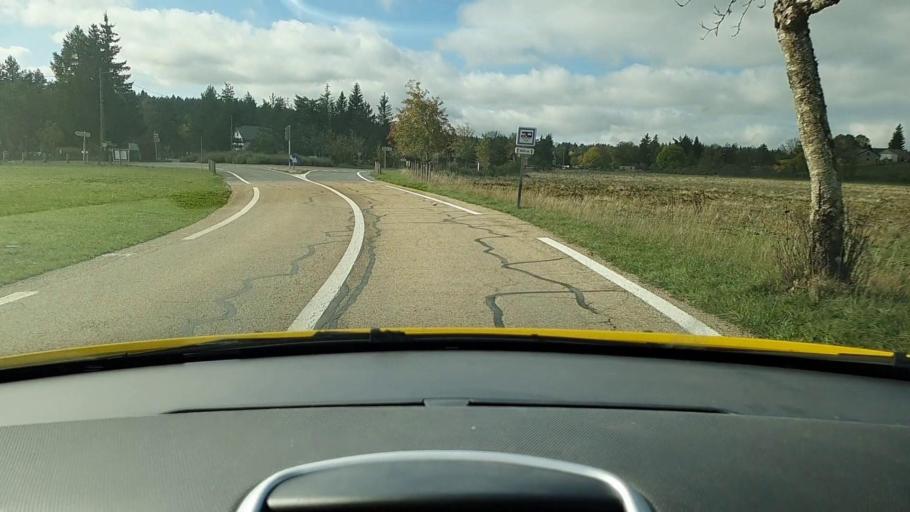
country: FR
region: Languedoc-Roussillon
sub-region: Departement de la Lozere
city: Meyrueis
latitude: 44.1147
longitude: 3.4851
